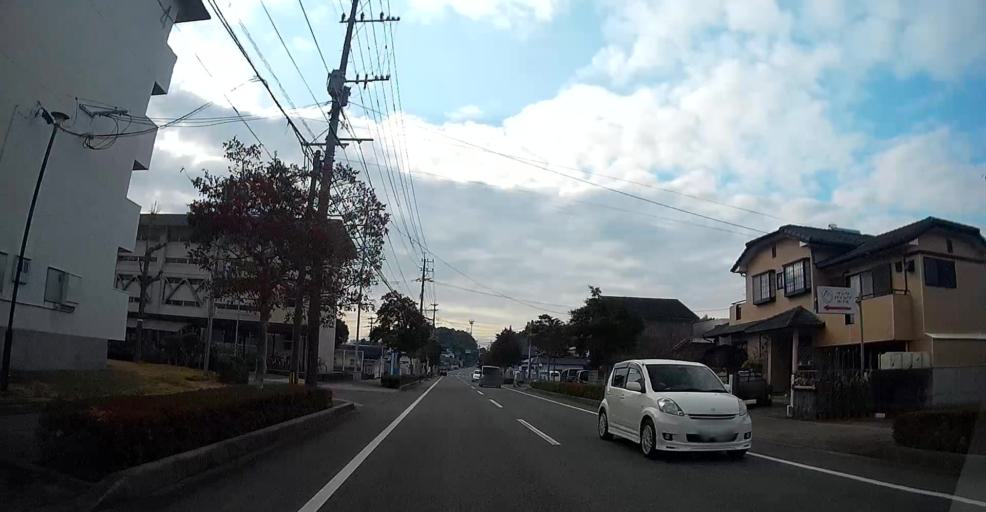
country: JP
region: Kumamoto
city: Hondo
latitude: 32.4420
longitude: 130.2033
